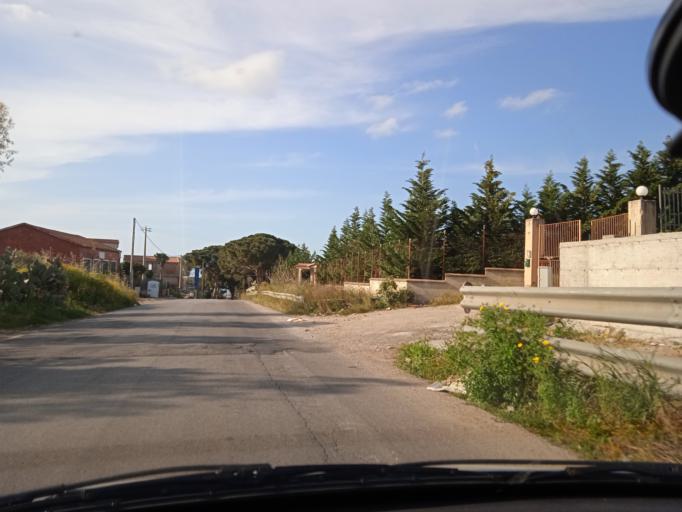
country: IT
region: Sicily
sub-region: Palermo
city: Portella di Mare
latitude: 38.0619
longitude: 13.4604
